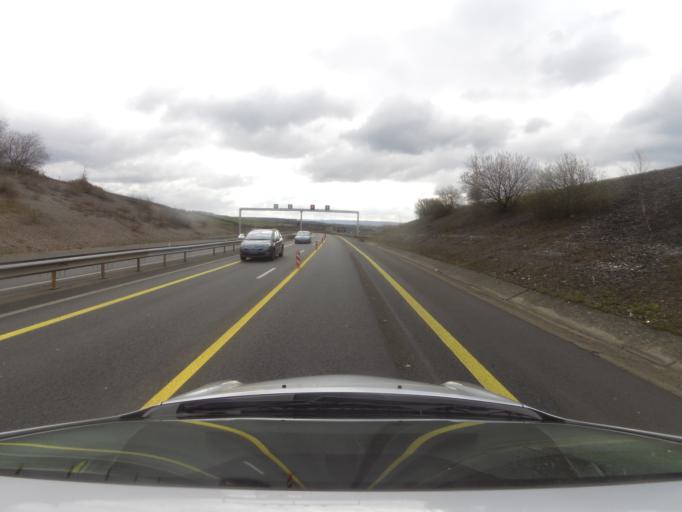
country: FR
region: Nord-Pas-de-Calais
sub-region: Departement du Pas-de-Calais
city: Isques
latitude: 50.6827
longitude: 1.6510
